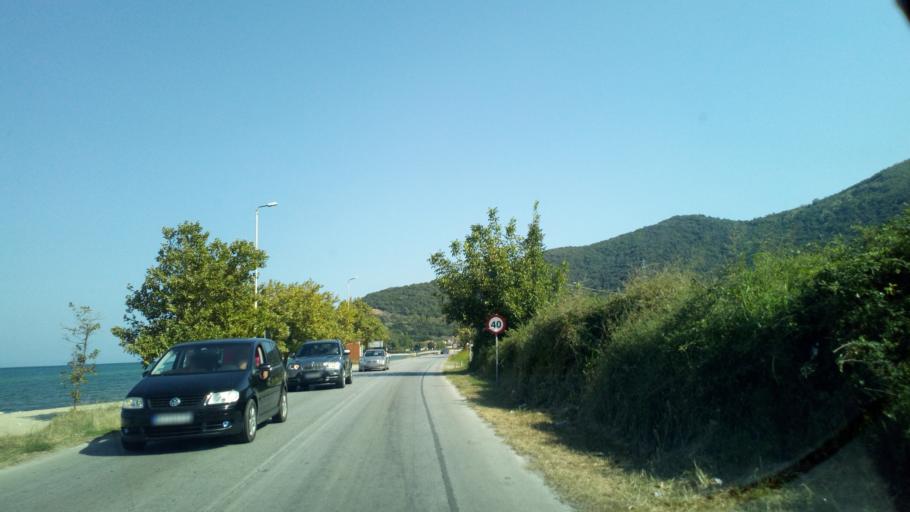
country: GR
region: Central Macedonia
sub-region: Nomos Thessalonikis
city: Stavros
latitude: 40.6600
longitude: 23.7257
